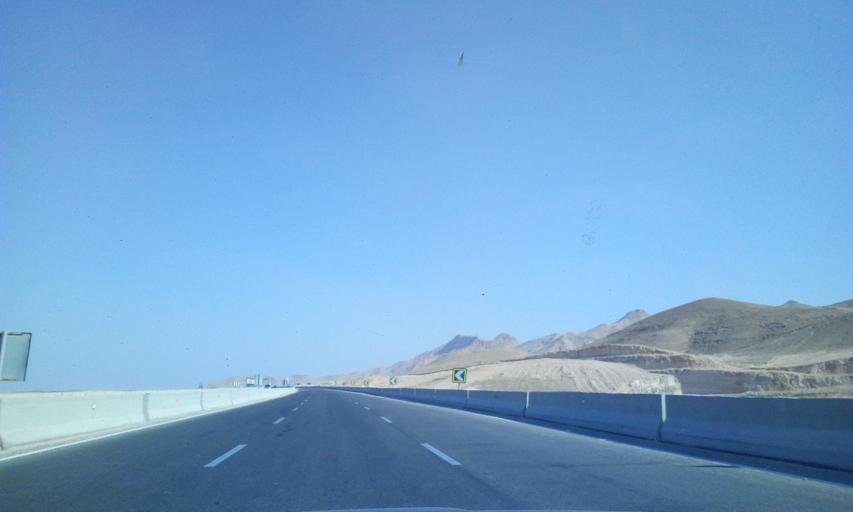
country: EG
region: As Suways
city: Ain Sukhna
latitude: 29.4533
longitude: 32.3364
